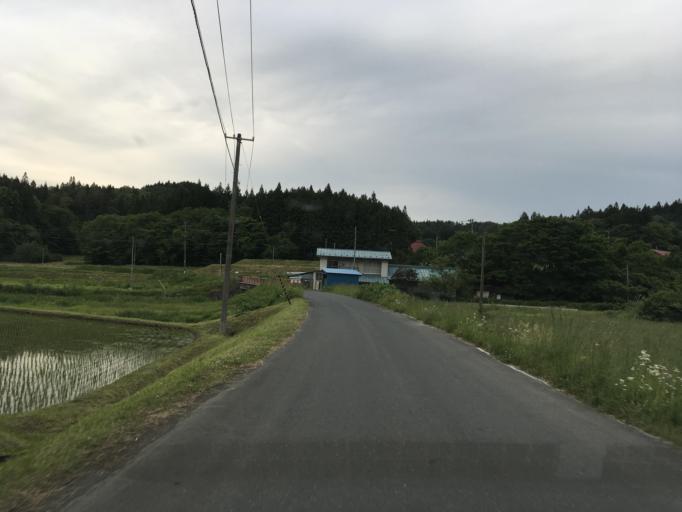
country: JP
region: Iwate
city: Mizusawa
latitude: 39.1628
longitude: 141.3102
